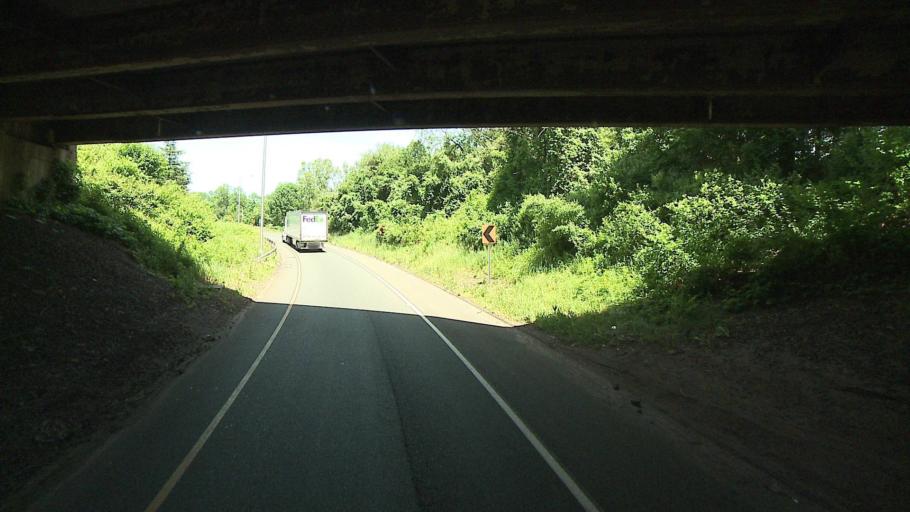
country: US
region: Connecticut
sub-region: New Haven County
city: Meriden
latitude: 41.5384
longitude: -72.7685
